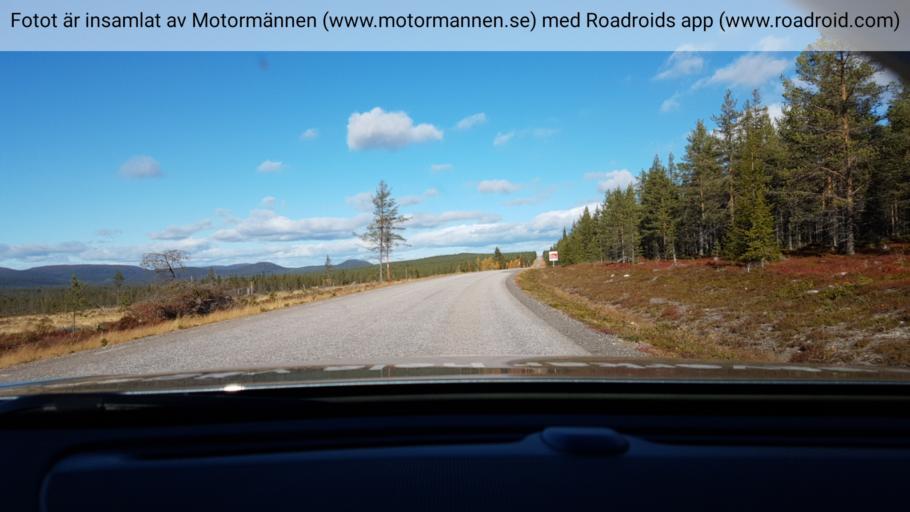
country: SE
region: Norrbotten
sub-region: Arjeplogs Kommun
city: Arjeplog
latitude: 65.8152
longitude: 18.4462
